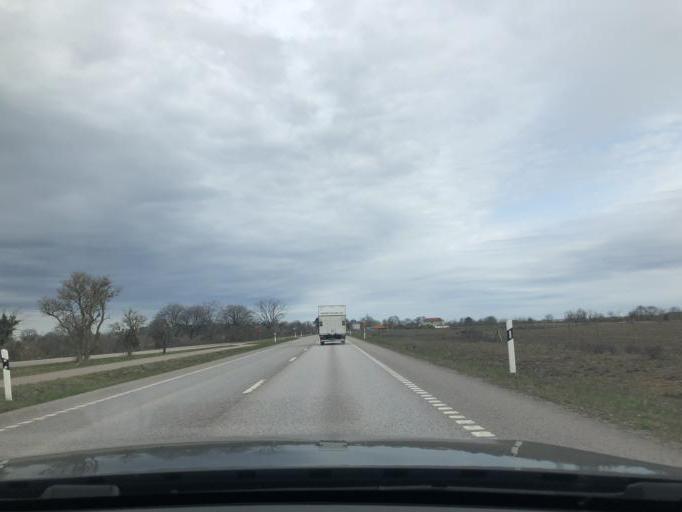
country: SE
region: Kalmar
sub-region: Borgholms Kommun
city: Borgholm
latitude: 56.8631
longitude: 16.6533
